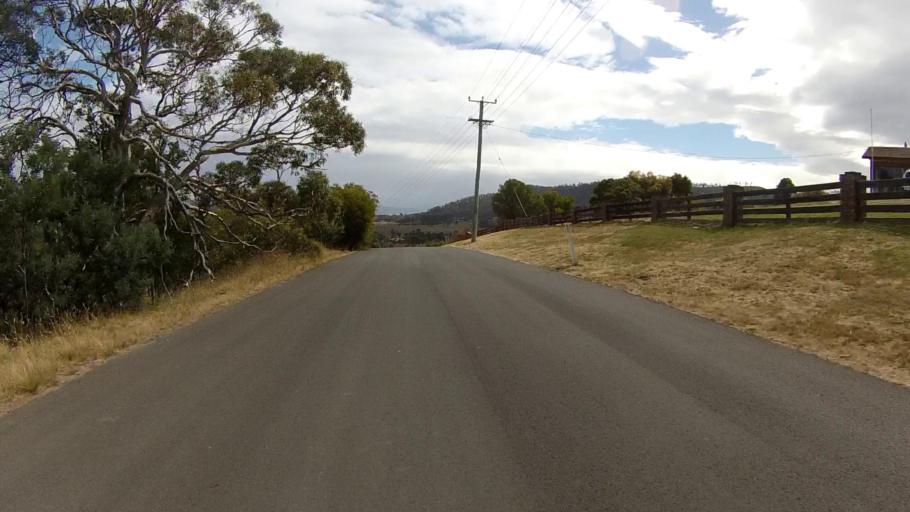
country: AU
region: Tasmania
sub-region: Clarence
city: Acton Park
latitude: -42.8847
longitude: 147.5019
